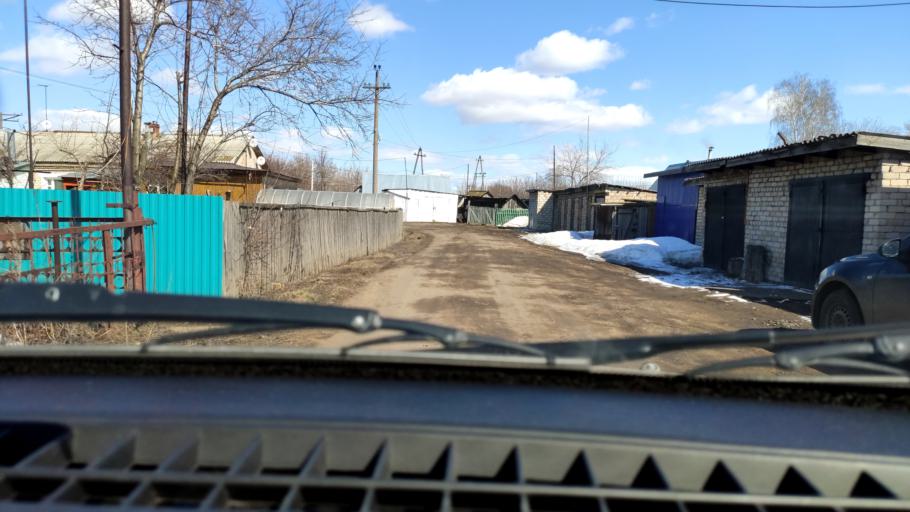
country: RU
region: Bashkortostan
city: Iglino
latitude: 54.8211
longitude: 56.3944
